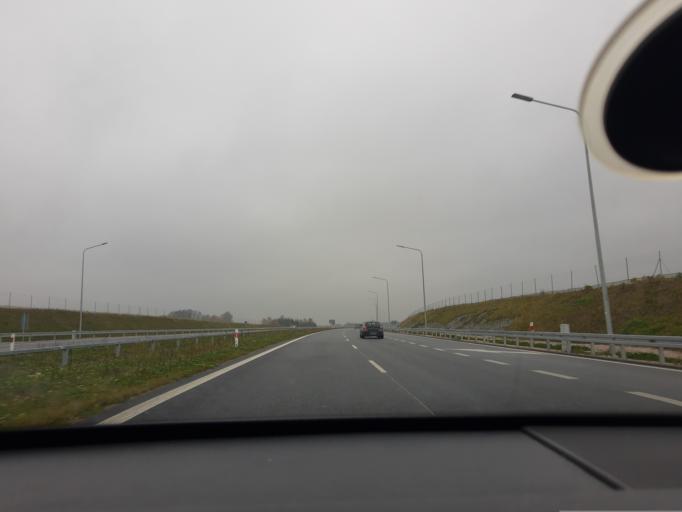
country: PL
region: Lodz Voivodeship
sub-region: Powiat pabianicki
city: Pabianice
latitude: 51.7027
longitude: 19.3412
